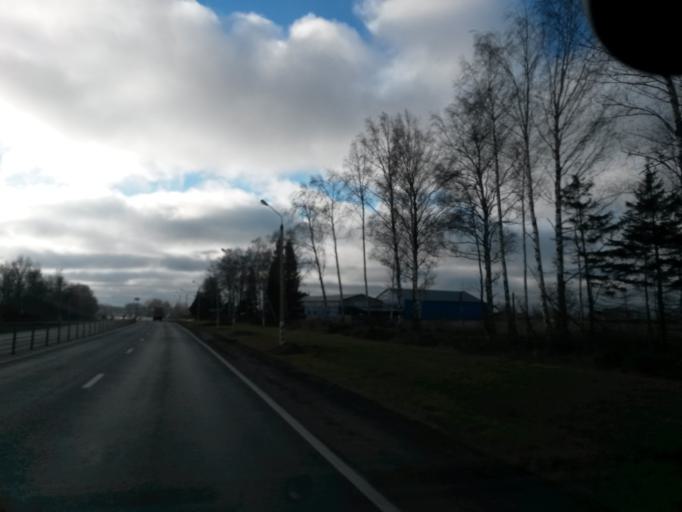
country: RU
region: Jaroslavl
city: Semibratovo
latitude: 57.3482
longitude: 39.5843
